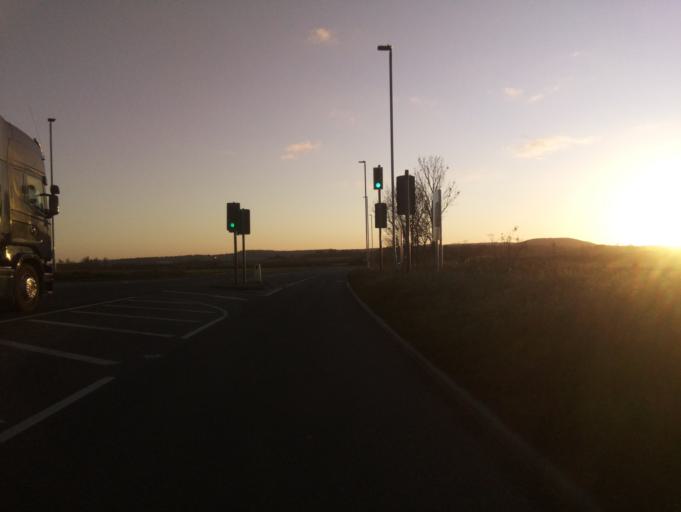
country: GB
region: England
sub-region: Wiltshire
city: Upton Scudamore
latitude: 51.2261
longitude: -2.1884
